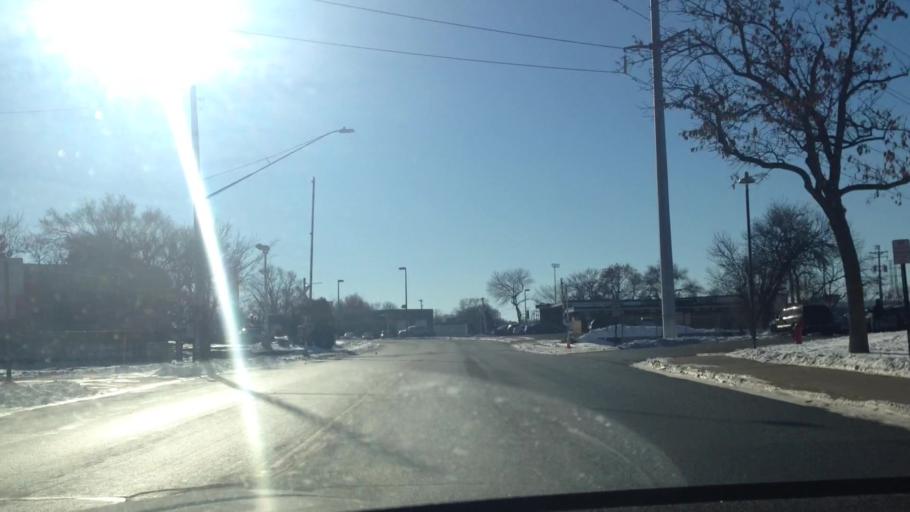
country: US
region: Minnesota
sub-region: Hennepin County
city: Saint Louis Park
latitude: 44.9432
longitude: -93.3604
